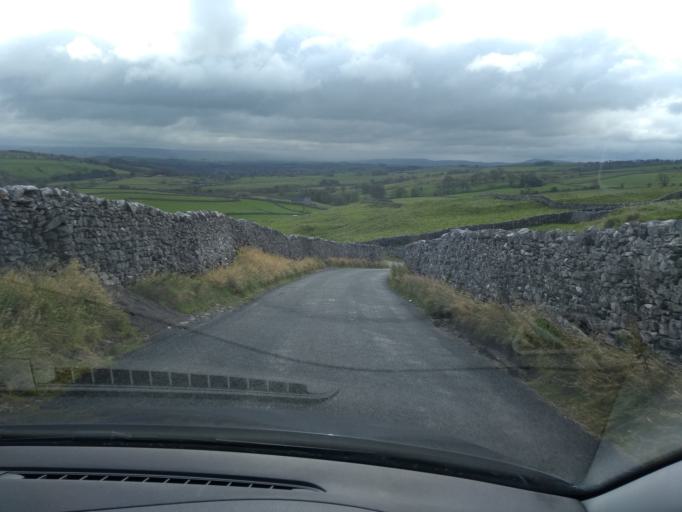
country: GB
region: England
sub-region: North Yorkshire
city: Gargrave
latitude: 54.0697
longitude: -2.1652
